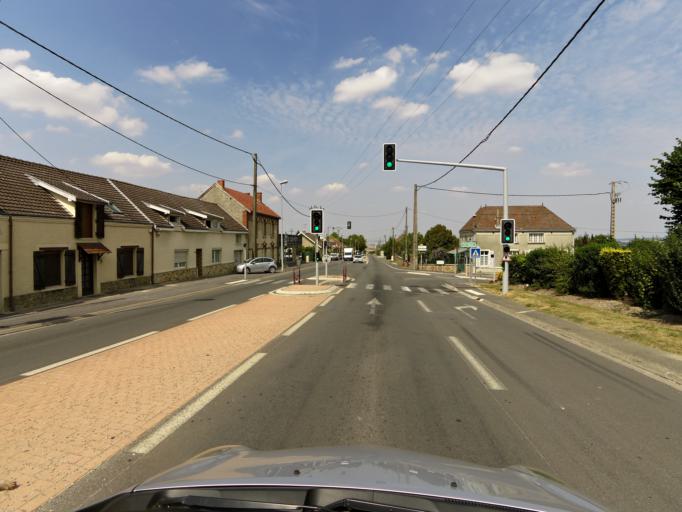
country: FR
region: Champagne-Ardenne
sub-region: Departement de la Marne
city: Rilly-la-Montagne
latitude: 49.1639
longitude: 4.0115
